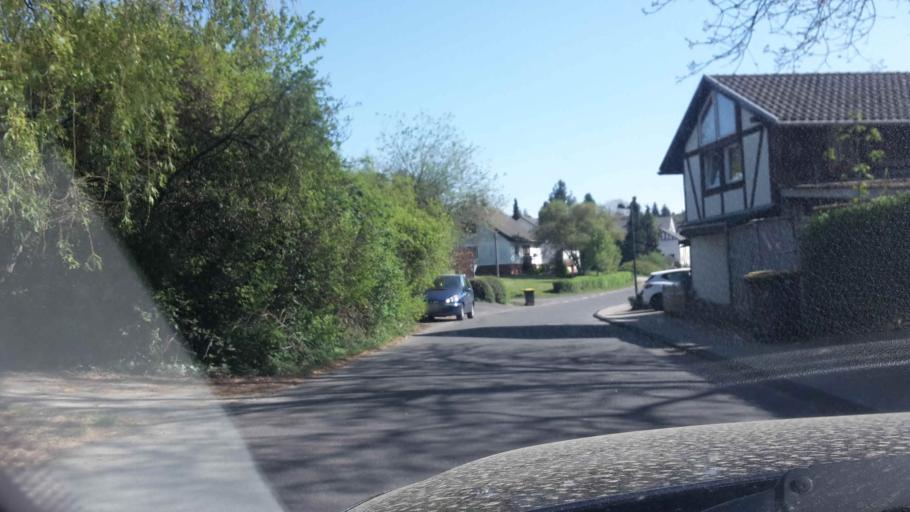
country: DE
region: Rheinland-Pfalz
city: Windhagen
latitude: 50.6694
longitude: 7.3372
